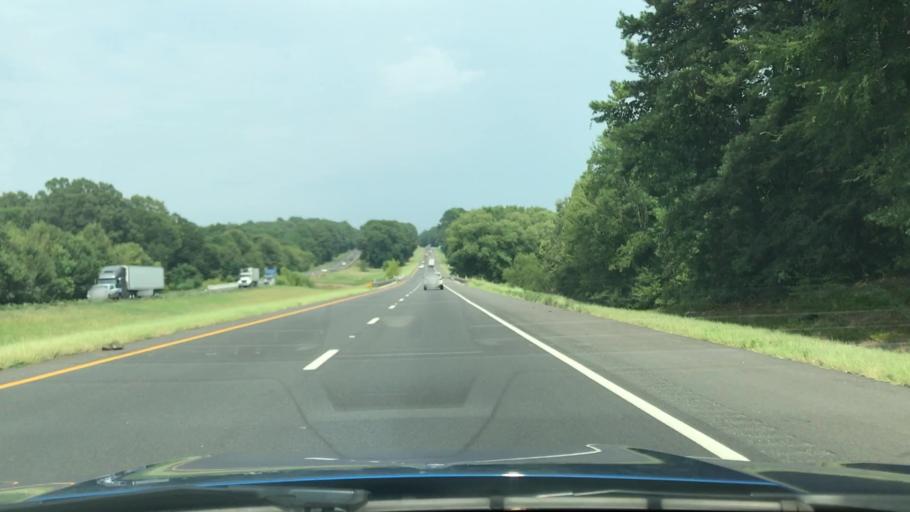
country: US
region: Texas
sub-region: Harrison County
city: Hallsville
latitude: 32.4688
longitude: -94.6066
